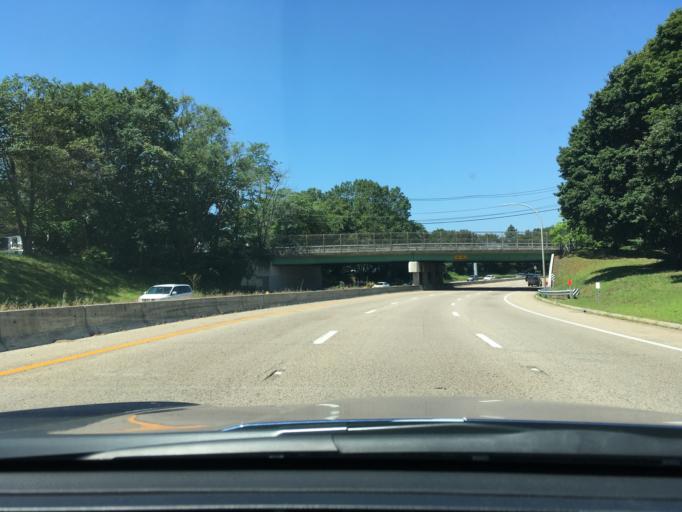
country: US
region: Rhode Island
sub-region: Providence County
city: Cranston
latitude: 41.7823
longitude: -71.4294
